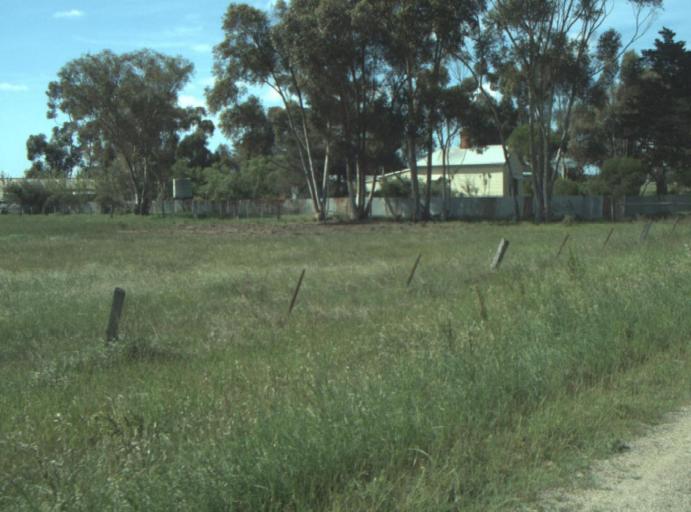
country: AU
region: Victoria
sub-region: Greater Geelong
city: Lara
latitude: -37.9863
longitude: 144.4217
